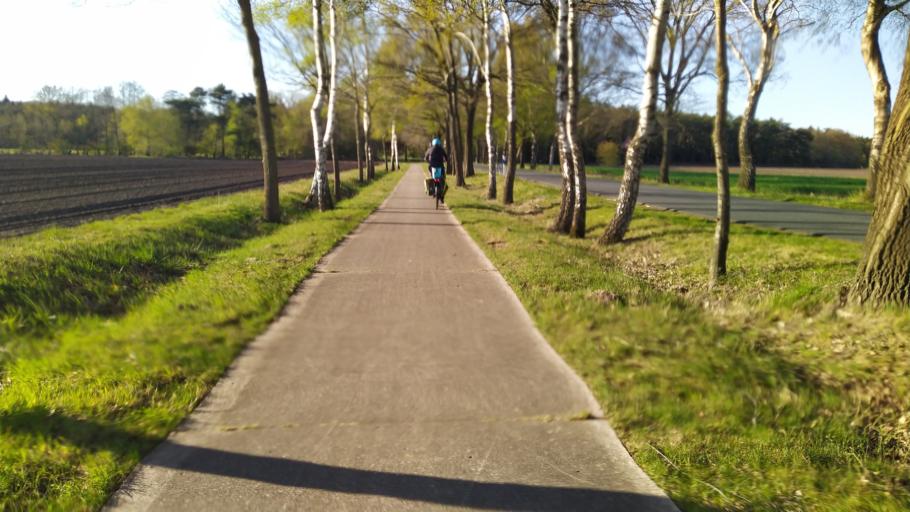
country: DE
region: Lower Saxony
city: Lengenbostel
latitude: 53.3101
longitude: 9.5093
